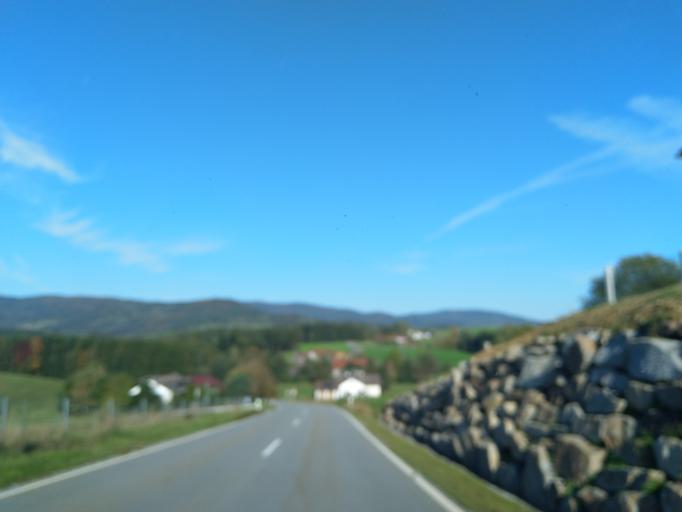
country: DE
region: Bavaria
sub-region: Lower Bavaria
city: Schwarzach
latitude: 48.9006
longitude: 12.8224
